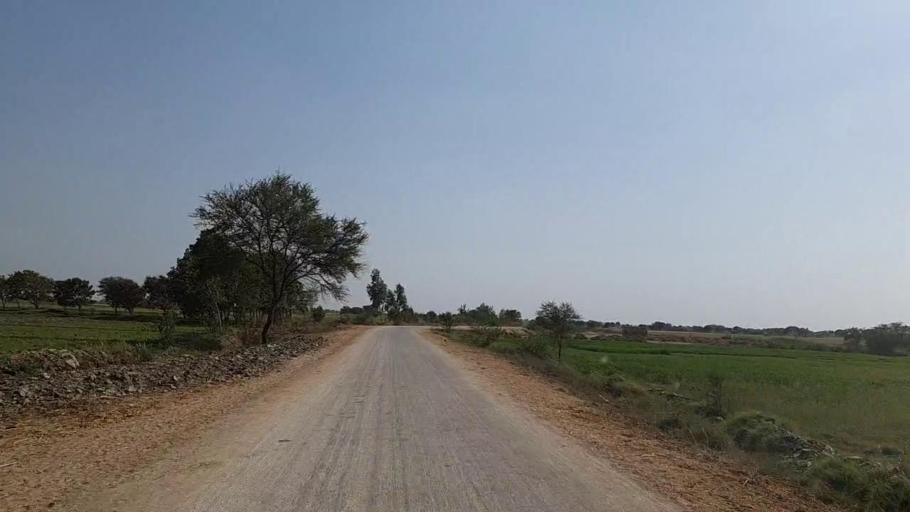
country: PK
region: Sindh
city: Daro Mehar
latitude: 24.7863
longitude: 68.1803
